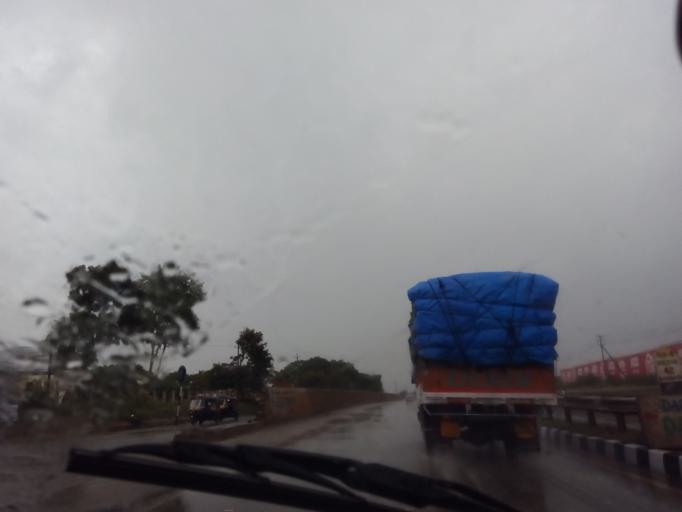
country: IN
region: Karnataka
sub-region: Chitradurga
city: Chitradurga
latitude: 14.2364
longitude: 76.3852
